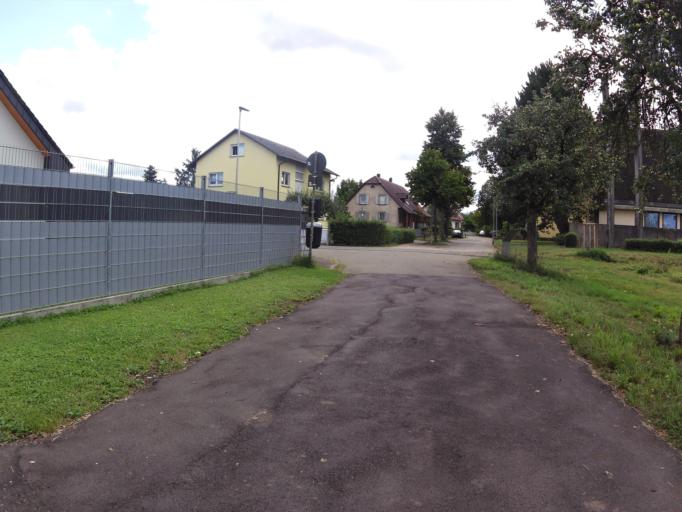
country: DE
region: Baden-Wuerttemberg
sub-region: Freiburg Region
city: Lahr
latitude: 48.3662
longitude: 7.8334
